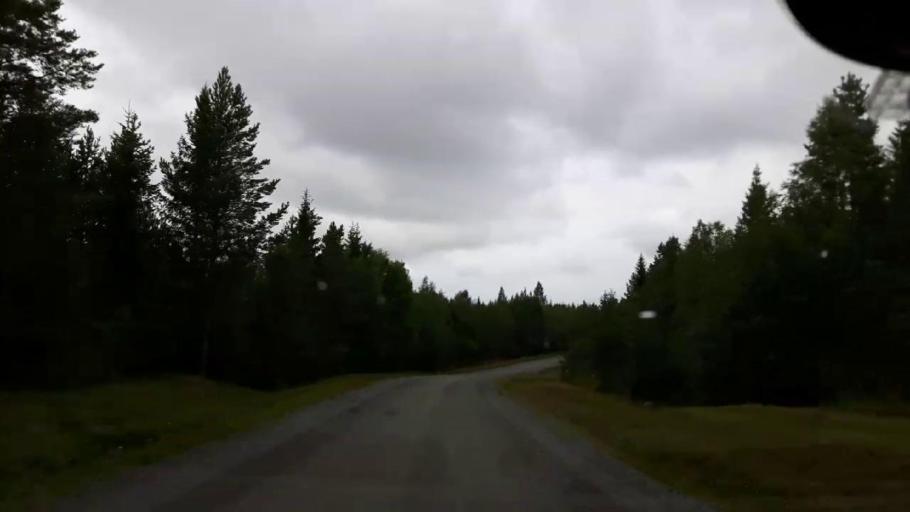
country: SE
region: Jaemtland
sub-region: OEstersunds Kommun
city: Ostersund
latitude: 63.0644
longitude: 14.5521
